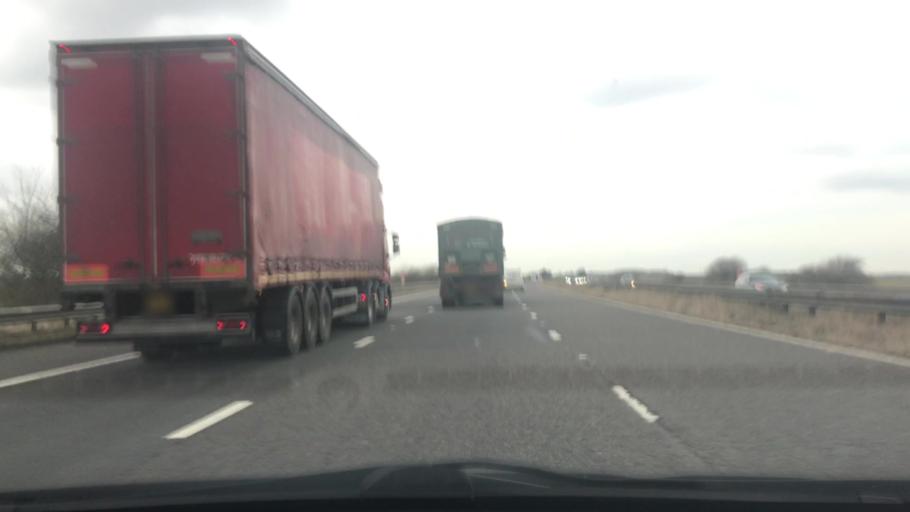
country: GB
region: England
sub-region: Doncaster
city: Hatfield
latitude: 53.5812
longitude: -0.9452
